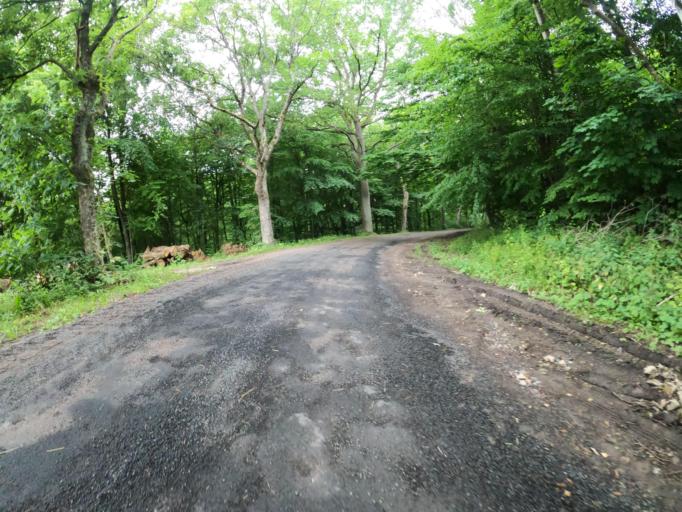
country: PL
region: West Pomeranian Voivodeship
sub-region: Powiat szczecinecki
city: Grzmiaca
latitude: 53.9323
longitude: 16.4576
